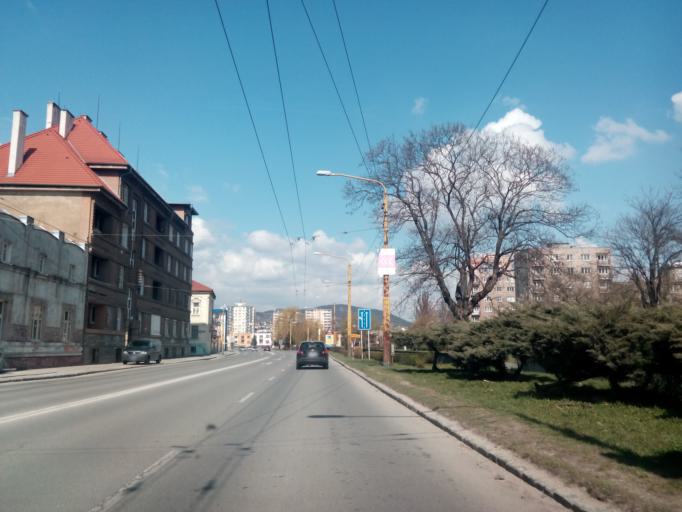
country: SK
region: Kosicky
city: Kosice
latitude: 48.7289
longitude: 21.2564
